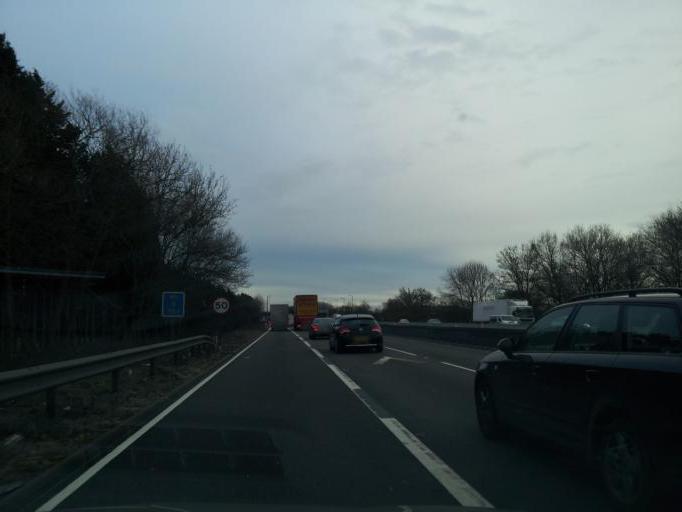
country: GB
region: England
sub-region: Northamptonshire
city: Long Buckby
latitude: 52.2586
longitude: -1.0831
